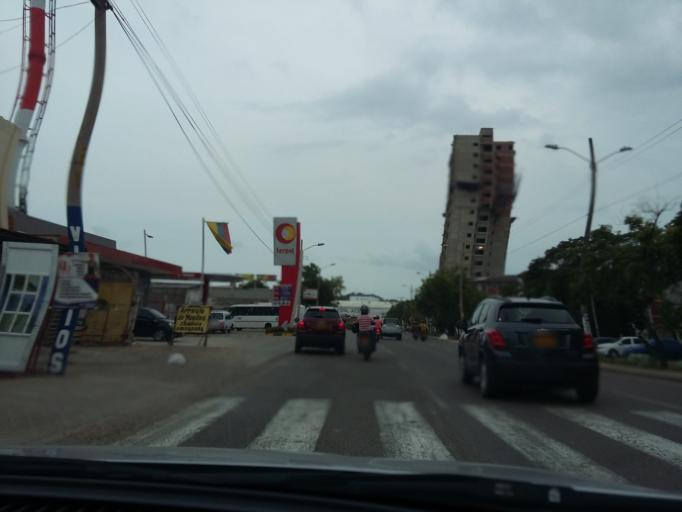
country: CO
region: Bolivar
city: Cartagena
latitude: 10.3860
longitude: -75.5013
